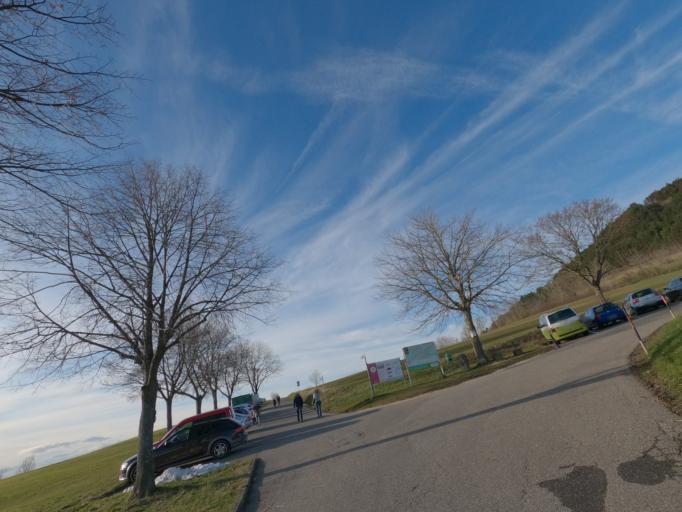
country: DE
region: Baden-Wuerttemberg
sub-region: Regierungsbezirk Stuttgart
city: Waldstetten
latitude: 48.7377
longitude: 9.8123
